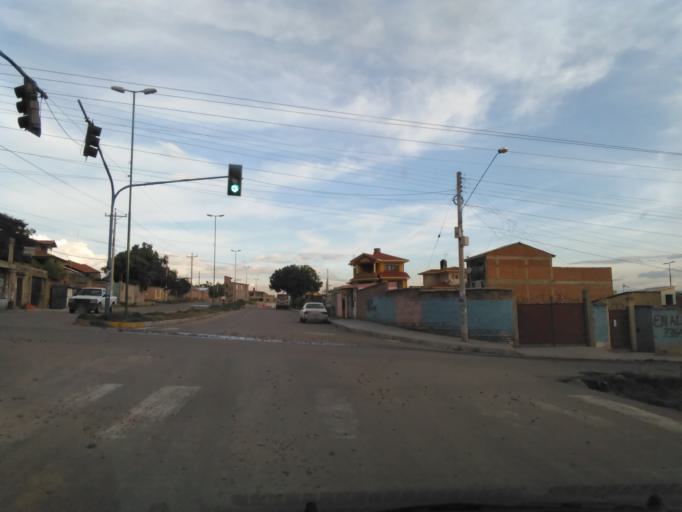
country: BO
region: Cochabamba
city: Cochabamba
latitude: -17.3449
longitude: -66.1753
